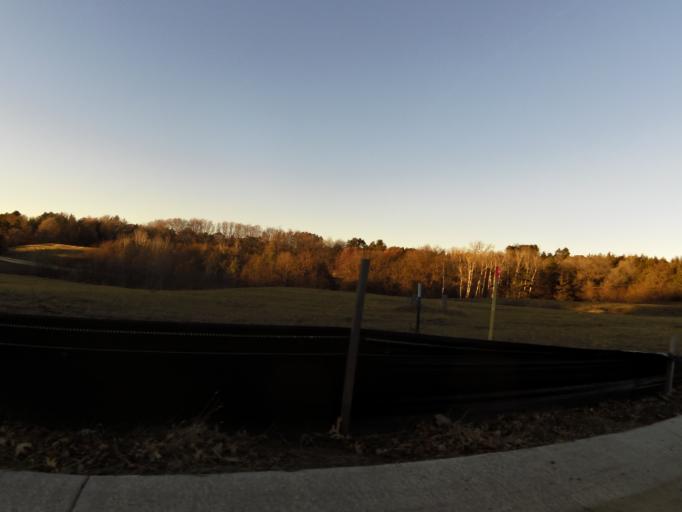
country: US
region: Wisconsin
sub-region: Saint Croix County
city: Hudson
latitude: 44.9701
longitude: -92.7280
